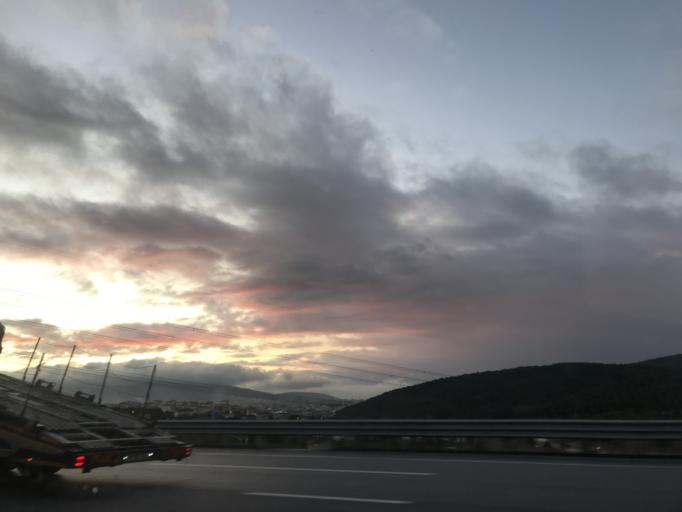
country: TR
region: Istanbul
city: Sultanbeyli
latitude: 40.9588
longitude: 29.3187
